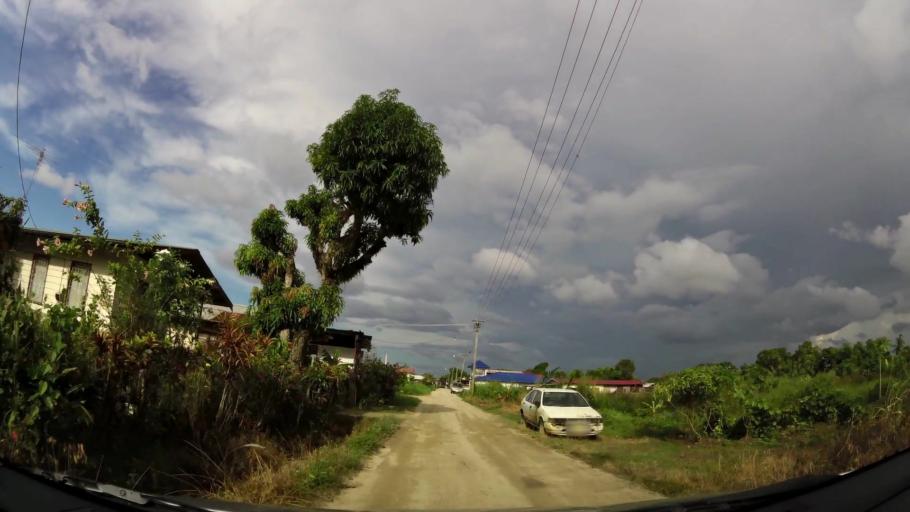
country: SR
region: Paramaribo
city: Paramaribo
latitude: 5.8462
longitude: -55.1832
